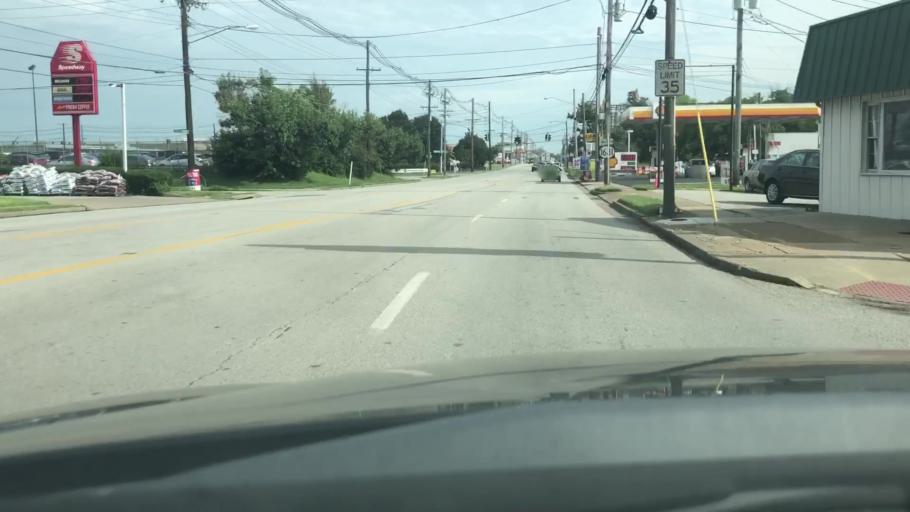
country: US
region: Kentucky
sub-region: Jefferson County
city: Audubon Park
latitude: 38.1928
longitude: -85.7509
